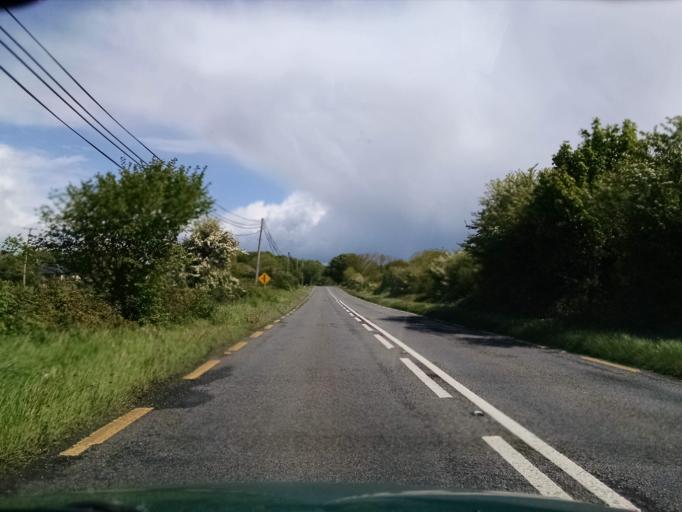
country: IE
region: Connaught
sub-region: County Galway
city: Oranmore
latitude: 53.1932
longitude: -8.8932
